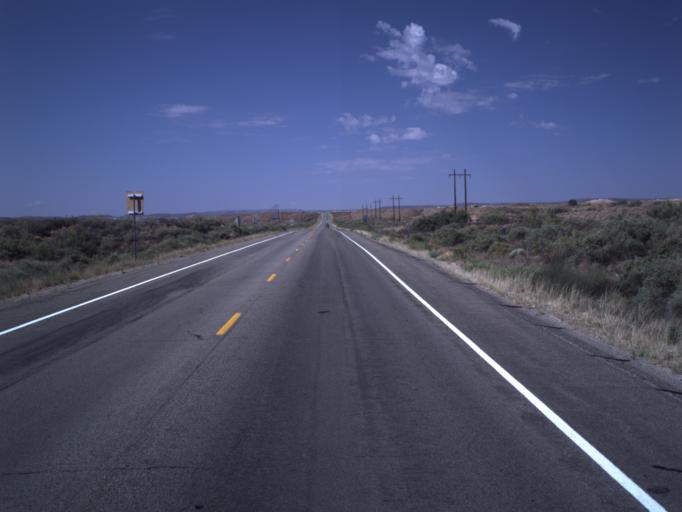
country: US
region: Utah
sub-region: San Juan County
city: Blanding
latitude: 37.2797
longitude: -109.5773
